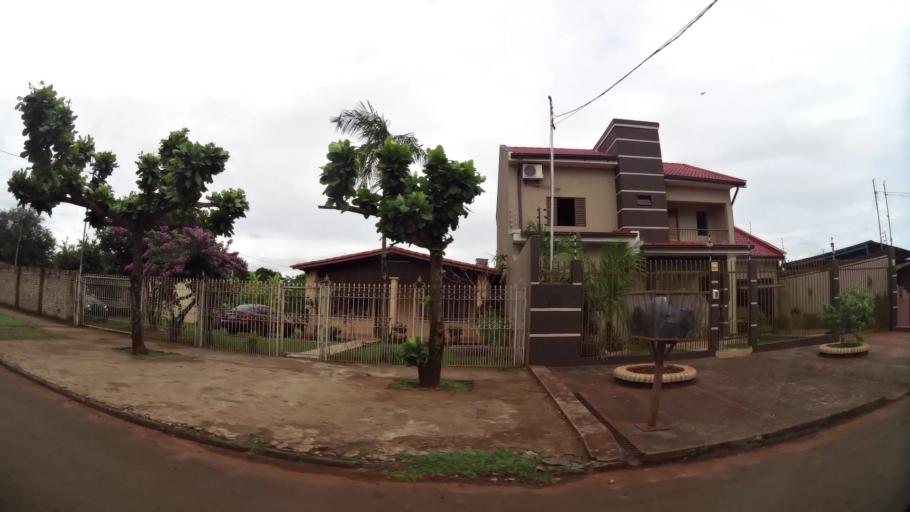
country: PY
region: Alto Parana
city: Ciudad del Este
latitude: -25.3989
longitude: -54.6391
